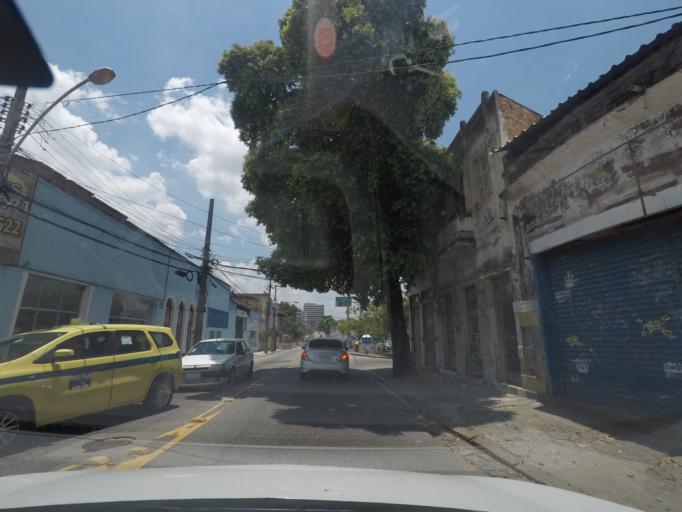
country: BR
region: Rio de Janeiro
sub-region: Rio De Janeiro
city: Rio de Janeiro
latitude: -22.8957
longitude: -43.3025
